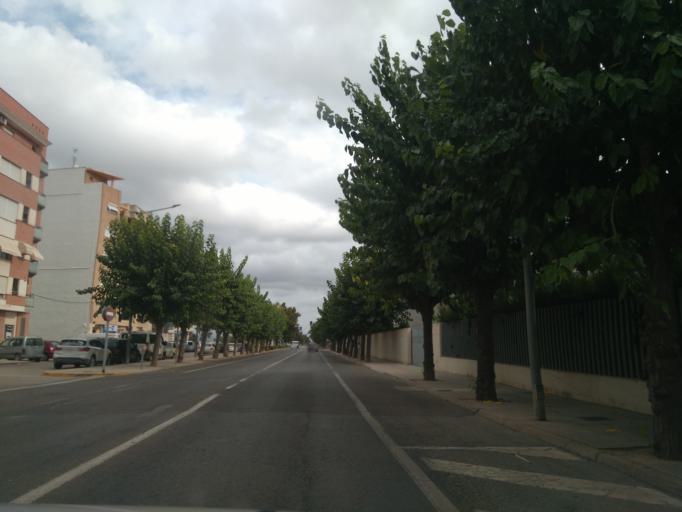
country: ES
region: Valencia
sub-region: Provincia de Valencia
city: Carlet
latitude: 39.2213
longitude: -0.5187
